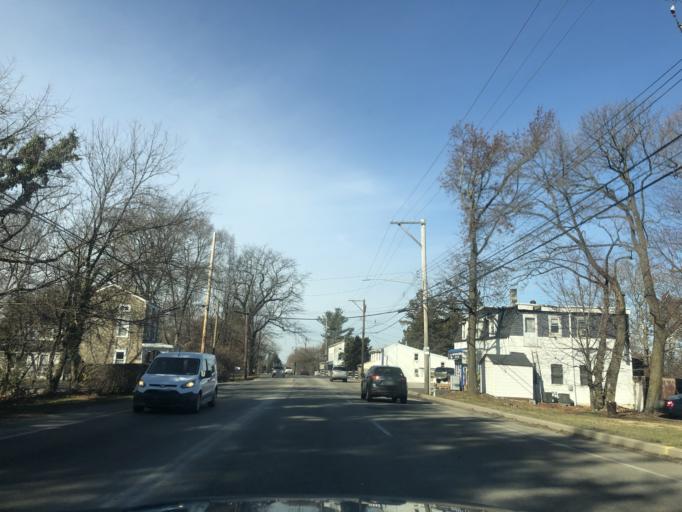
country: US
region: Pennsylvania
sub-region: Montgomery County
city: Plymouth Meeting
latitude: 40.0743
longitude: -75.2441
